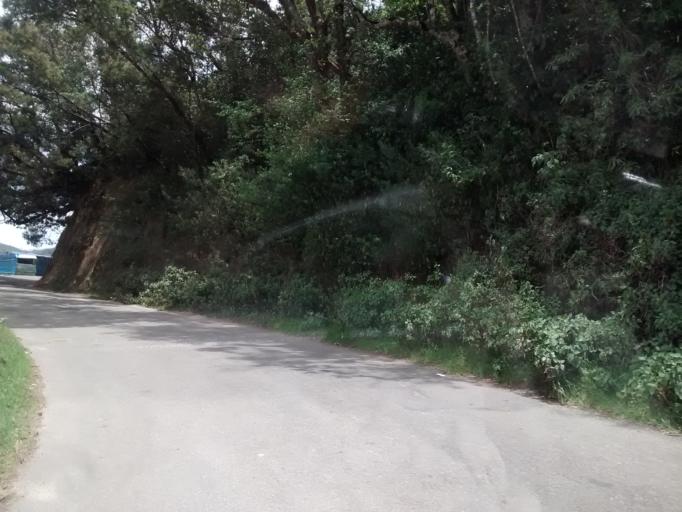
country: IN
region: Tamil Nadu
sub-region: Theni
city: Bodinayakkanur
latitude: 10.1301
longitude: 77.2287
